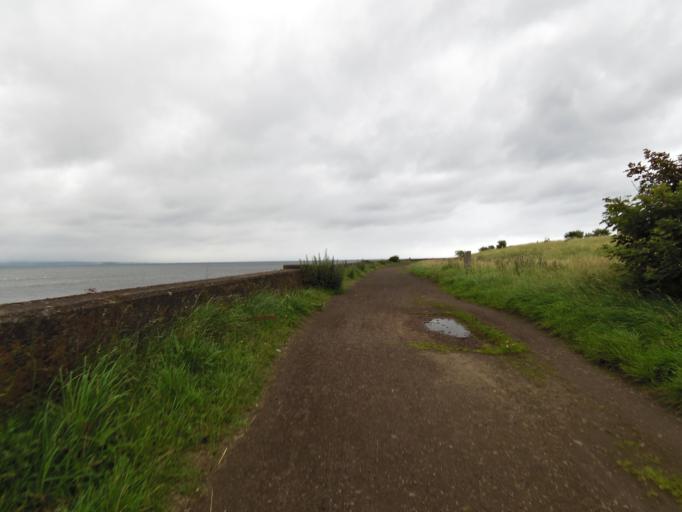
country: GB
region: Scotland
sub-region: East Lothian
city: Musselburgh
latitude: 55.9508
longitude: -3.0485
